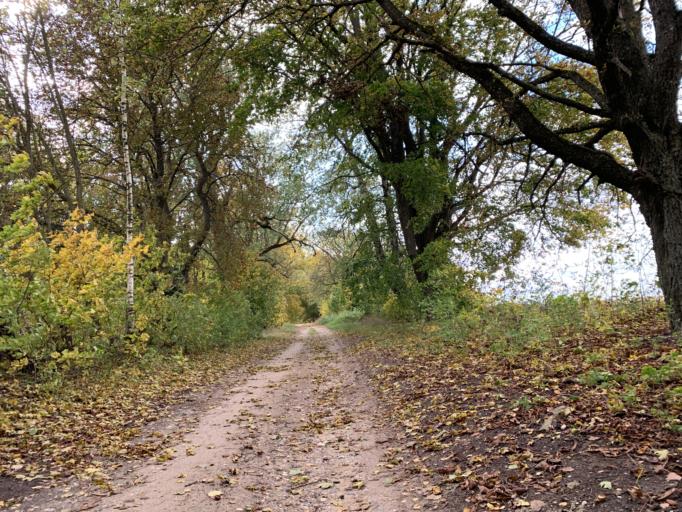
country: BY
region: Minsk
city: Nyasvizh
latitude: 53.2343
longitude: 26.7044
